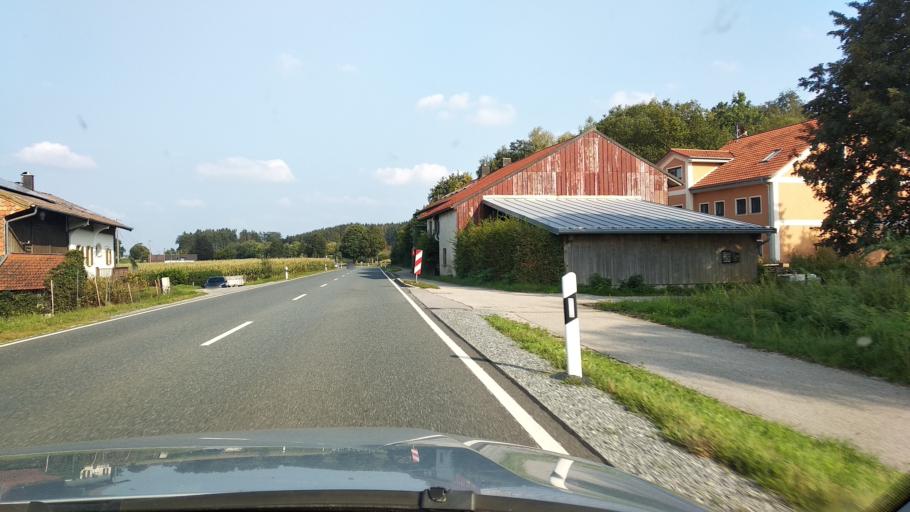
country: DE
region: Bavaria
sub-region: Upper Bavaria
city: Steinhoring
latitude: 48.0838
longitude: 12.0424
